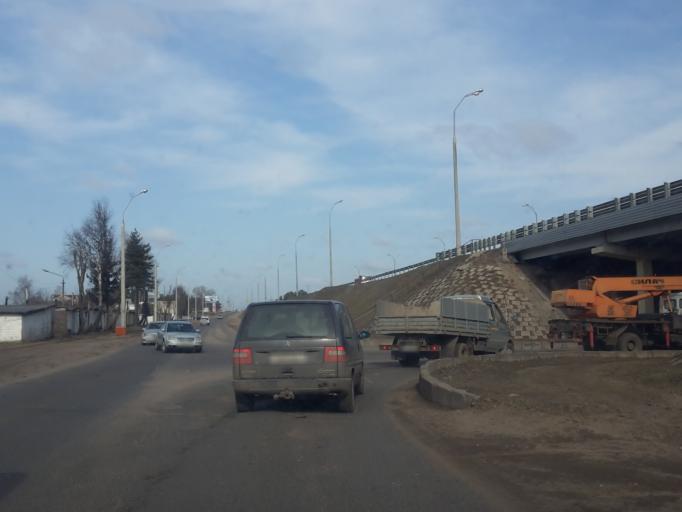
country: BY
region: Minsk
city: Vyaliki Trastsyanets
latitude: 53.9091
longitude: 27.6856
